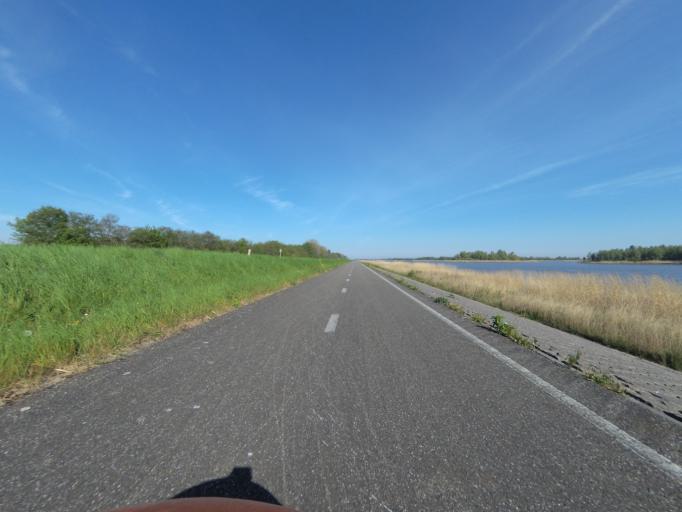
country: NL
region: Overijssel
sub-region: Gemeente Kampen
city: Kampen
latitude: 52.5609
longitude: 5.8375
